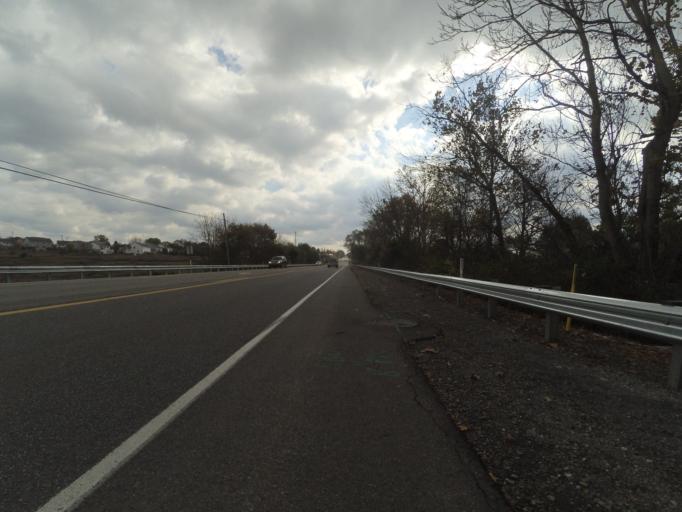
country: US
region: Pennsylvania
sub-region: Centre County
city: Bellefonte
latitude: 40.8974
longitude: -77.7885
